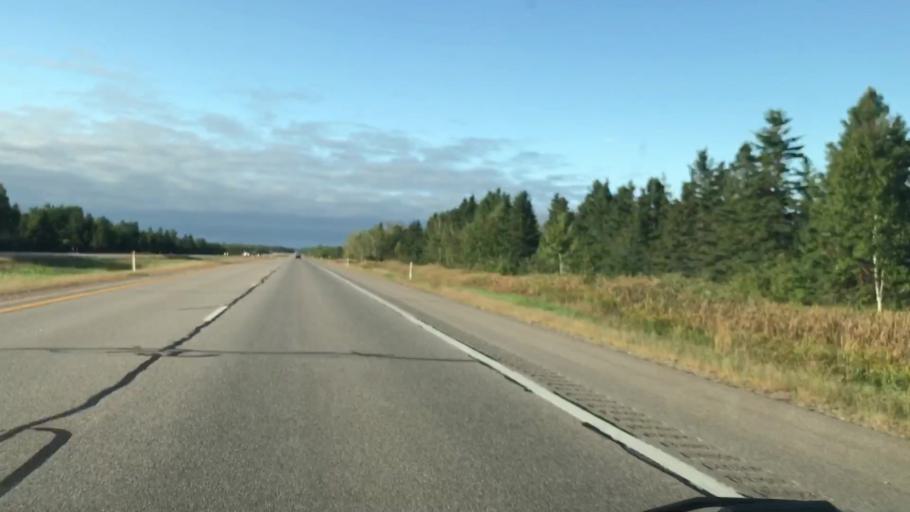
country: US
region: Michigan
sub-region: Chippewa County
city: Sault Ste. Marie
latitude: 46.4156
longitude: -84.3969
